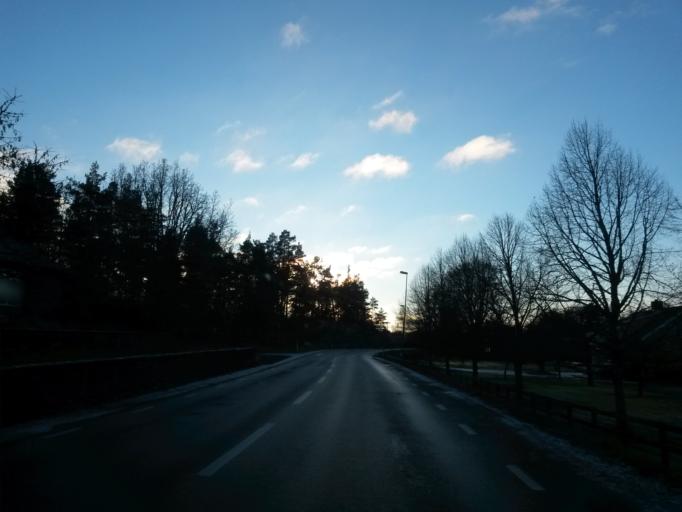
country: SE
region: Vaestra Goetaland
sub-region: Essunga Kommun
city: Nossebro
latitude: 58.2306
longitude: 12.7224
